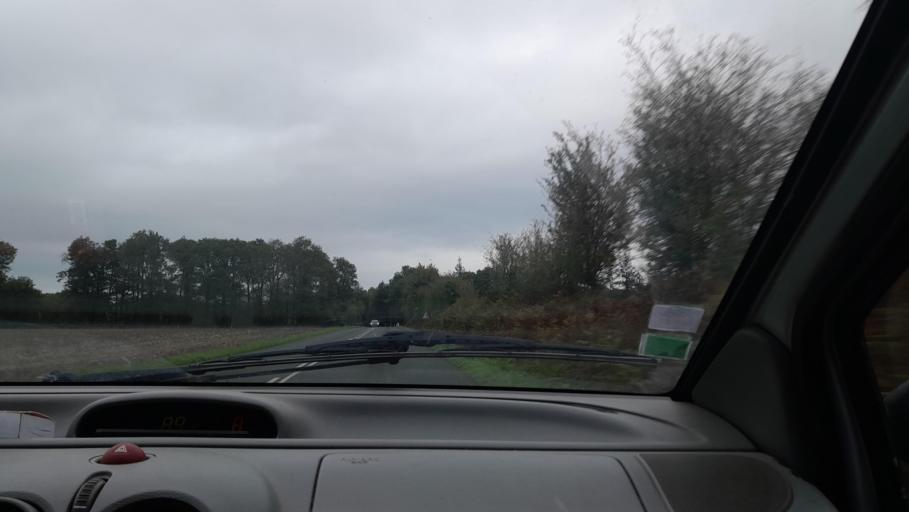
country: FR
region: Pays de la Loire
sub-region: Departement de Maine-et-Loire
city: Pouance
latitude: 47.6997
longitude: -1.1825
